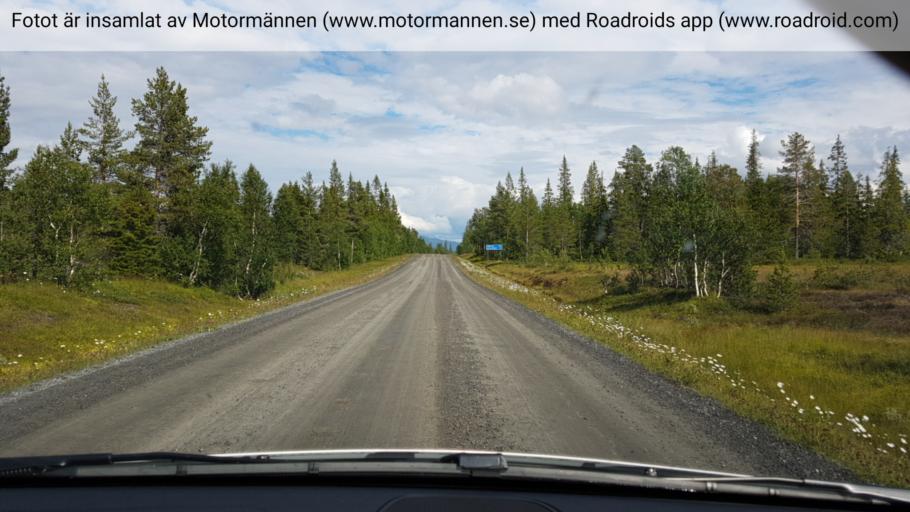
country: NO
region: Nord-Trondelag
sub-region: Snasa
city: Snaase
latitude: 63.7092
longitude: 12.3702
